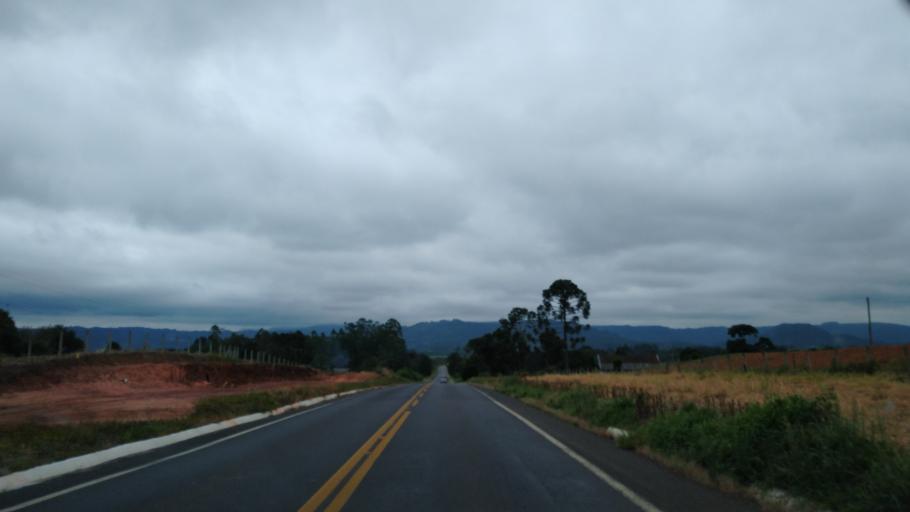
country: BR
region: Santa Catarina
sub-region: Porto Uniao
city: Porto Uniao
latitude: -26.2828
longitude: -51.0059
